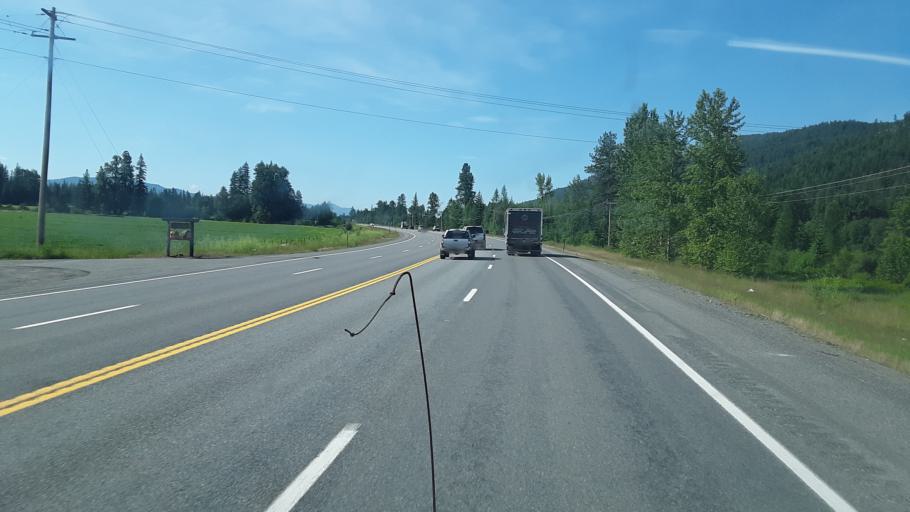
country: US
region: Idaho
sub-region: Bonner County
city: Ponderay
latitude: 48.3755
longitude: -116.5466
